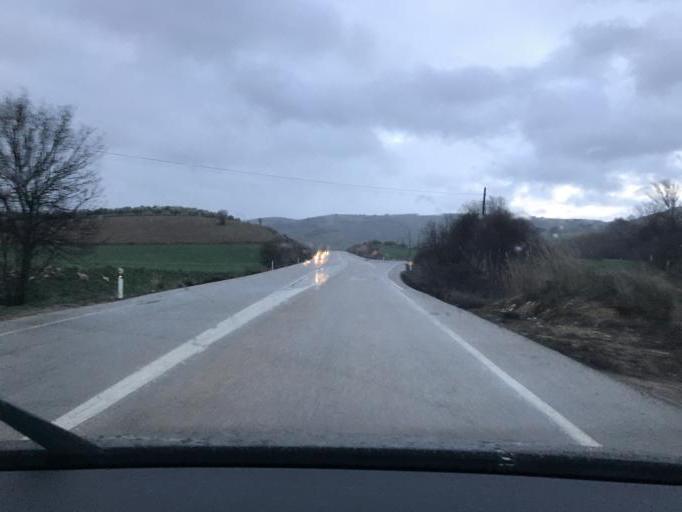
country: ES
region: Andalusia
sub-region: Provincia de Granada
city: Campotejar
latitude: 37.4539
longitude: -3.6293
